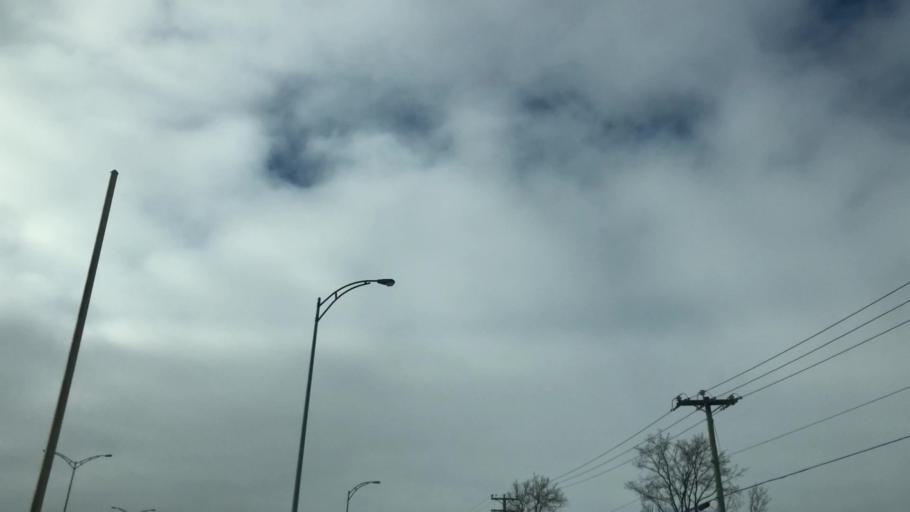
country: CA
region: Quebec
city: Sainte-Anne-de-Bellevue
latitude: 45.4221
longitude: -73.9633
